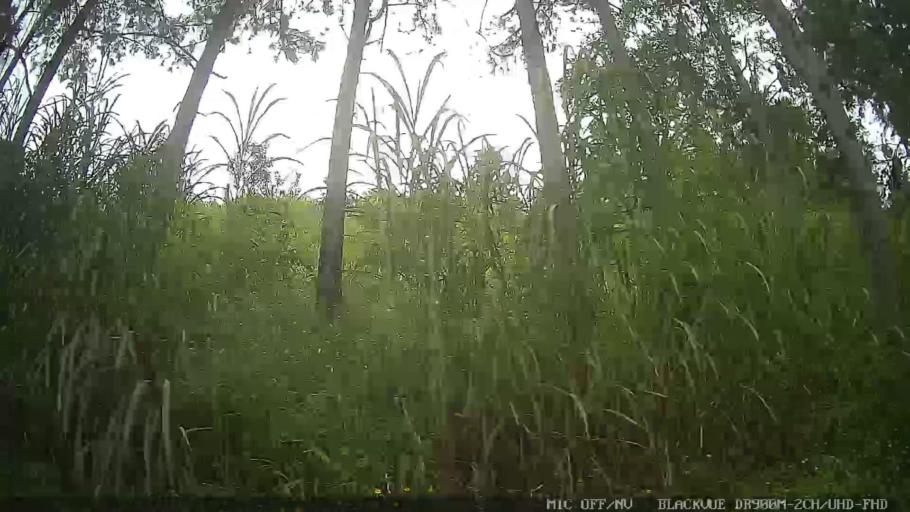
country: BR
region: Sao Paulo
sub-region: Santa Isabel
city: Santa Isabel
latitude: -23.3667
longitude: -46.2489
